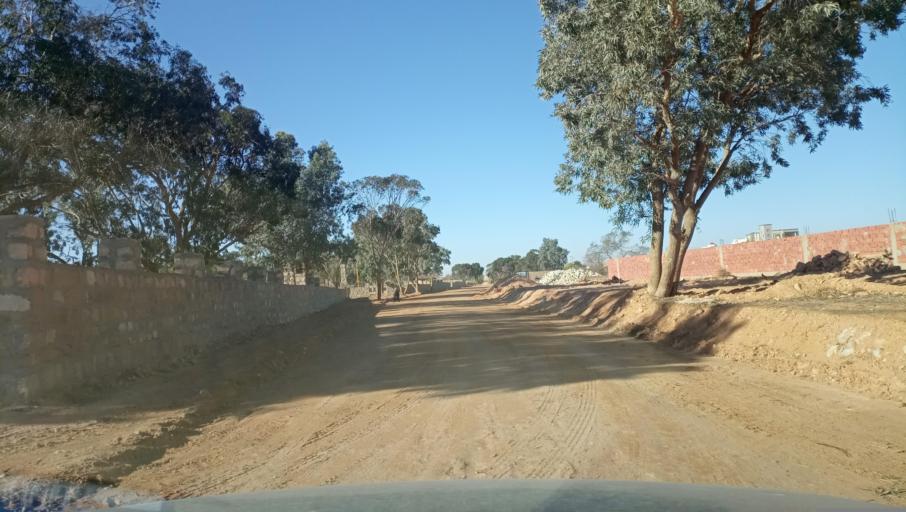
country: TN
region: Madanin
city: Medenine
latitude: 33.1812
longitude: 10.4418
